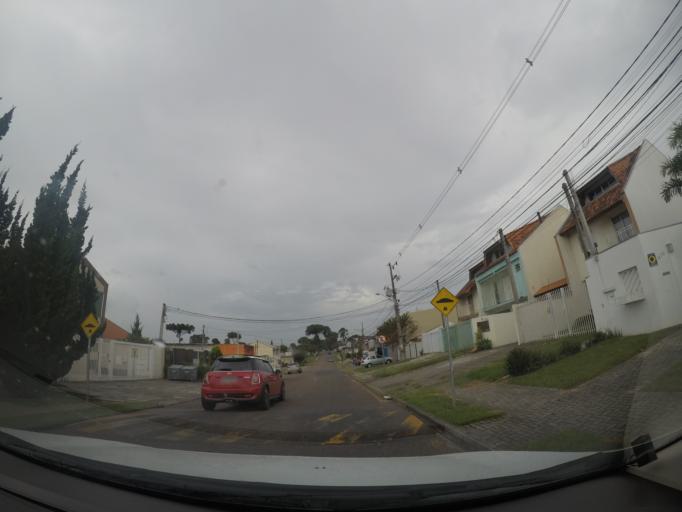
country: BR
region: Parana
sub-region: Sao Jose Dos Pinhais
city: Sao Jose dos Pinhais
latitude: -25.5104
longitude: -49.2482
